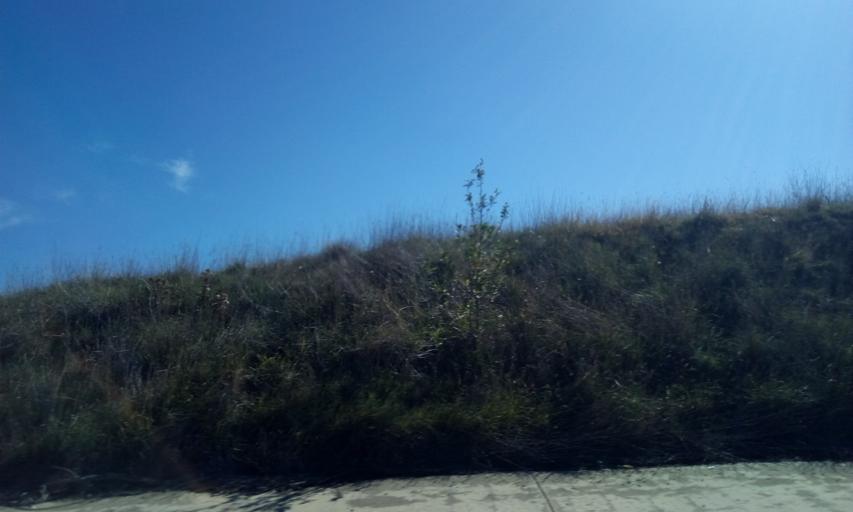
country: AU
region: New South Wales
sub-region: Yass Valley
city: Gundaroo
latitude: -35.1208
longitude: 149.3462
